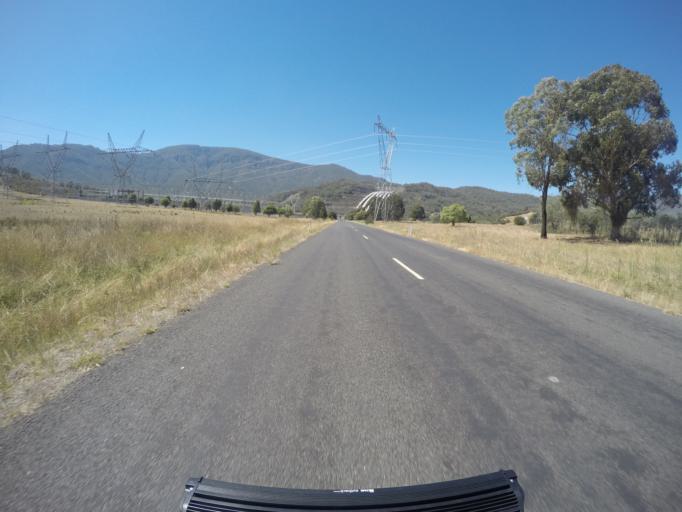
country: AU
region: New South Wales
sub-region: Tumut Shire
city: Tumut
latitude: -35.6062
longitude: 148.2851
